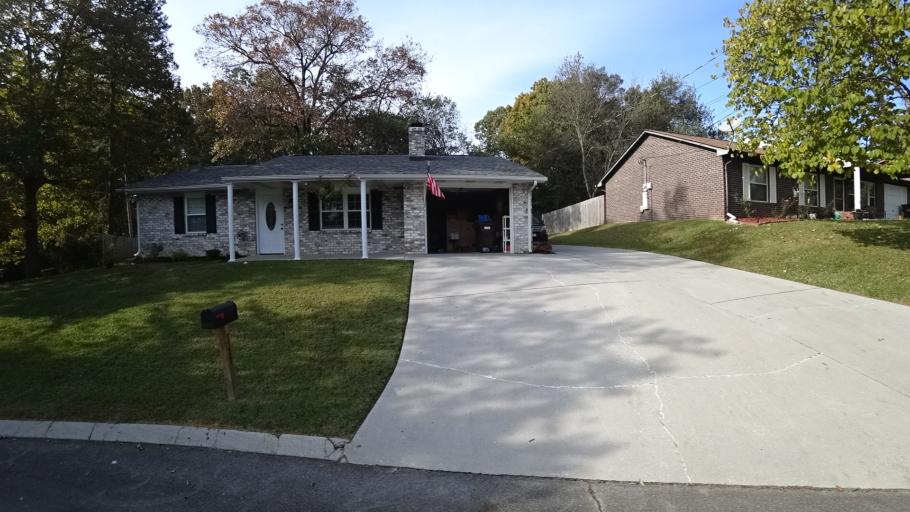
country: US
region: Tennessee
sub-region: Knox County
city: Farragut
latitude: 35.9099
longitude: -84.1652
